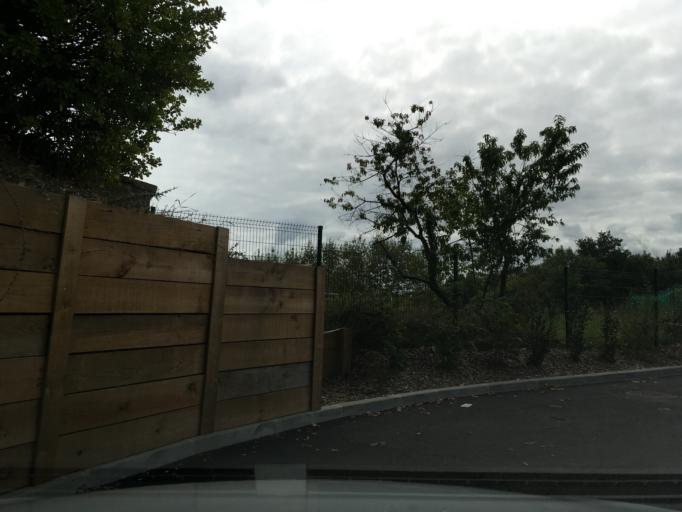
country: FR
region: Aquitaine
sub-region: Departement des Pyrenees-Atlantiques
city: Bayonne
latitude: 43.4830
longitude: -1.4584
